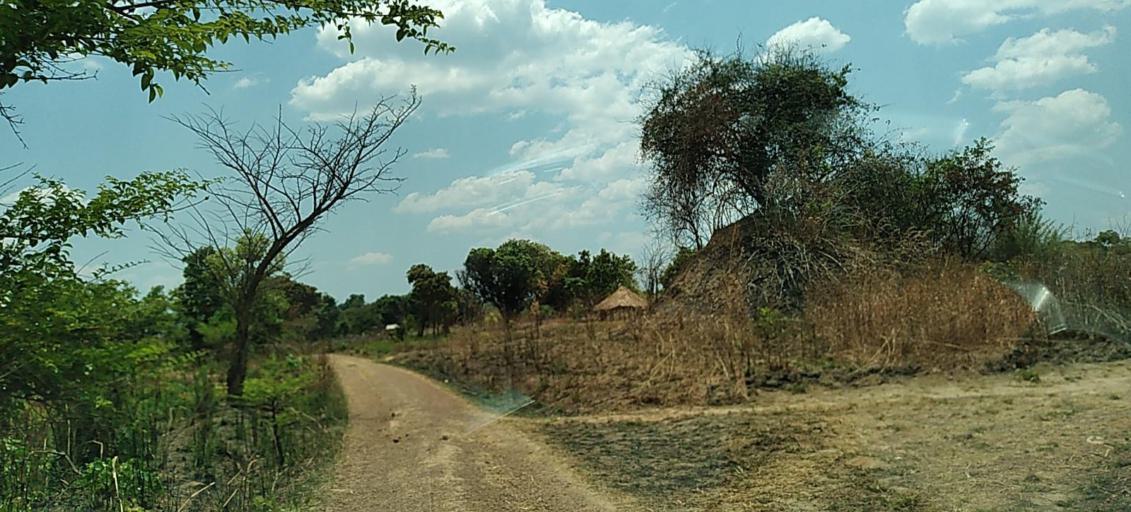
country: ZM
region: Copperbelt
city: Chililabombwe
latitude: -12.4662
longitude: 27.6677
